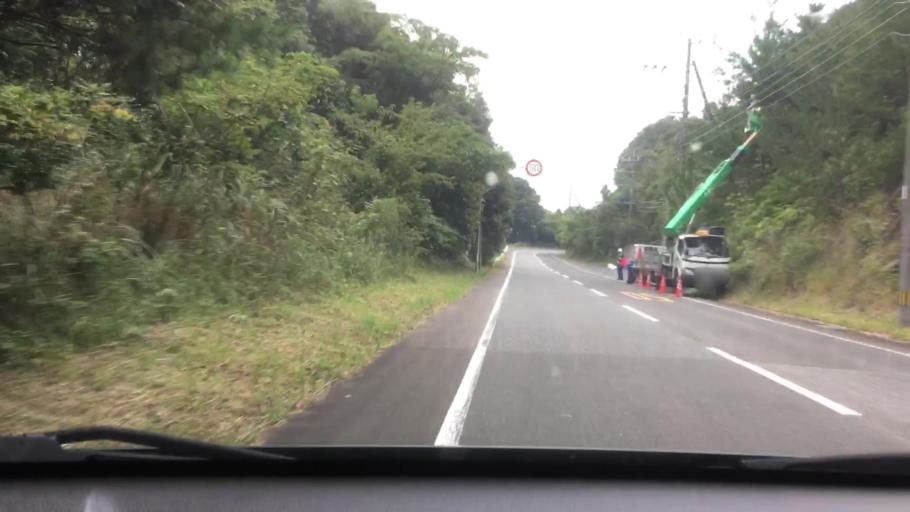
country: JP
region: Nagasaki
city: Sasebo
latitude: 32.9751
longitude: 129.7045
